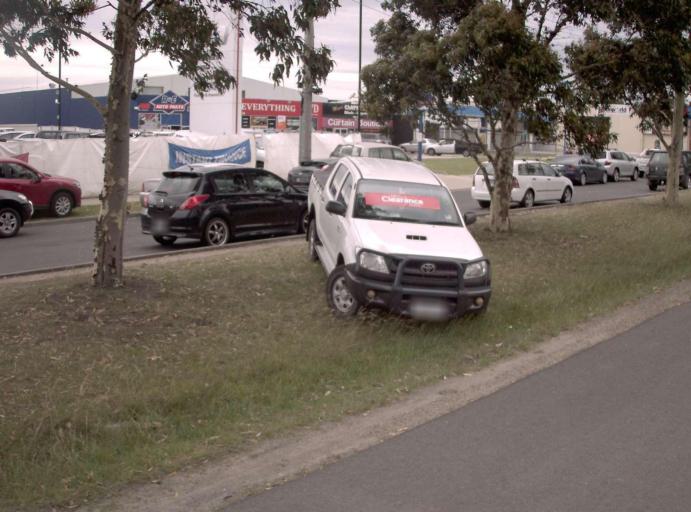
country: AU
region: Victoria
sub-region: Casey
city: Cranbourne
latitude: -38.0950
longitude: 145.2822
